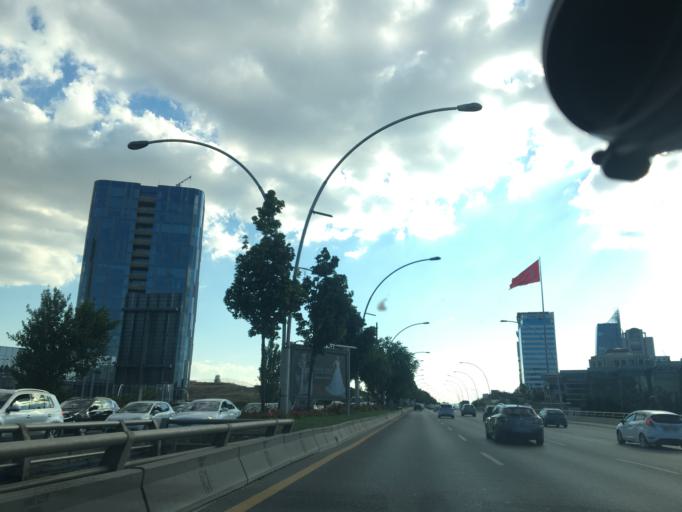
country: TR
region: Ankara
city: Ankara
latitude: 39.9106
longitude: 32.8055
